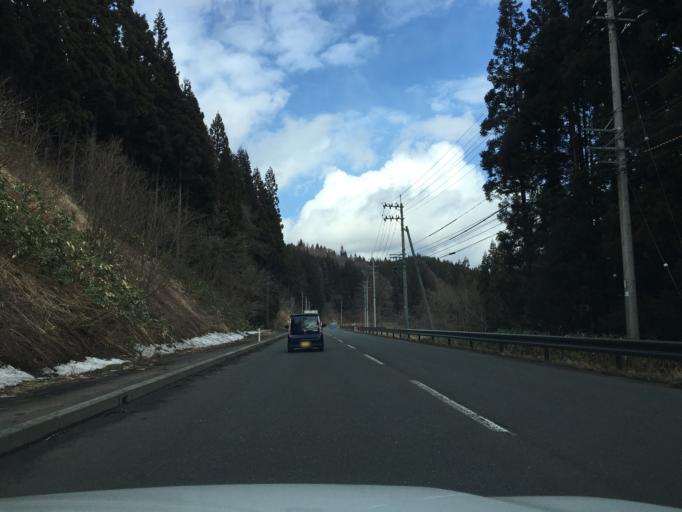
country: JP
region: Akita
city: Takanosu
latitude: 40.0954
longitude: 140.3411
